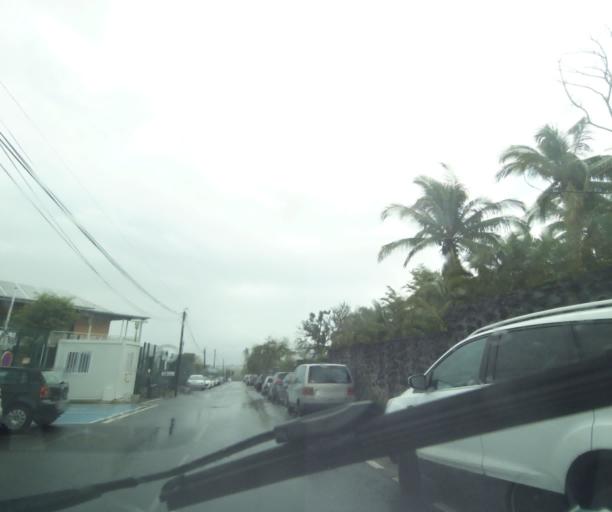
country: RE
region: Reunion
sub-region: Reunion
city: Le Port
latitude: -20.9746
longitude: 55.3020
